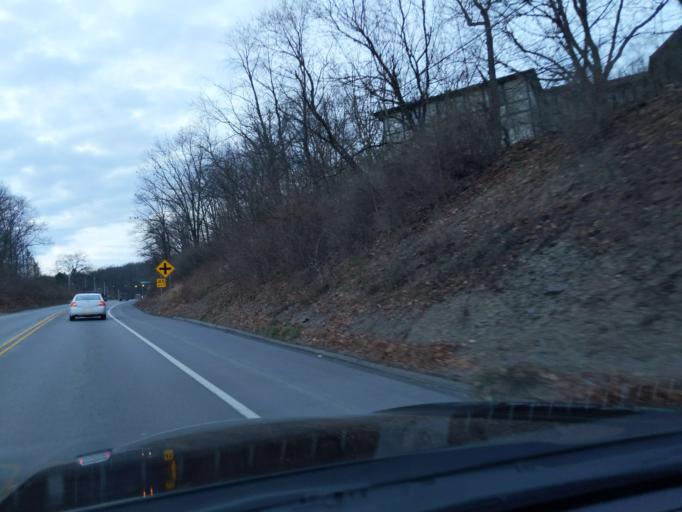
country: US
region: Pennsylvania
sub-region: Blair County
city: Lakemont
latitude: 40.4608
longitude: -78.3628
